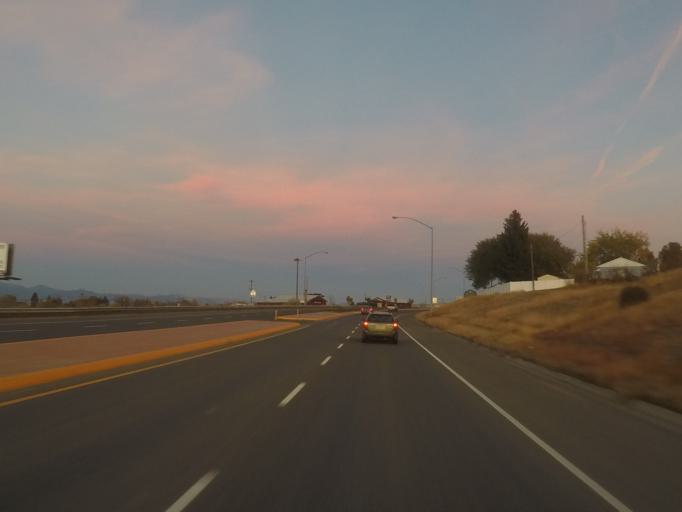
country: US
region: Montana
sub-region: Lewis and Clark County
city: Helena West Side
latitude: 46.6073
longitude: -112.0750
